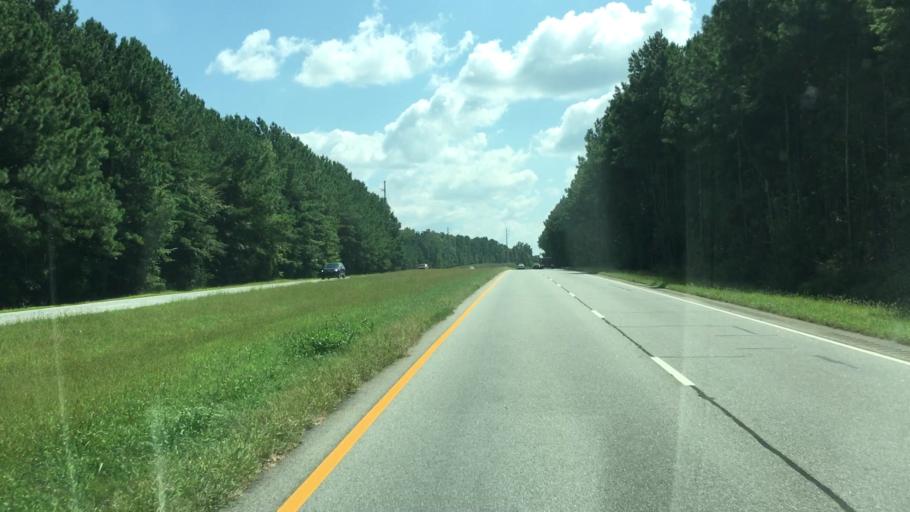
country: US
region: Georgia
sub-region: Morgan County
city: Madison
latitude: 33.5836
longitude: -83.4475
